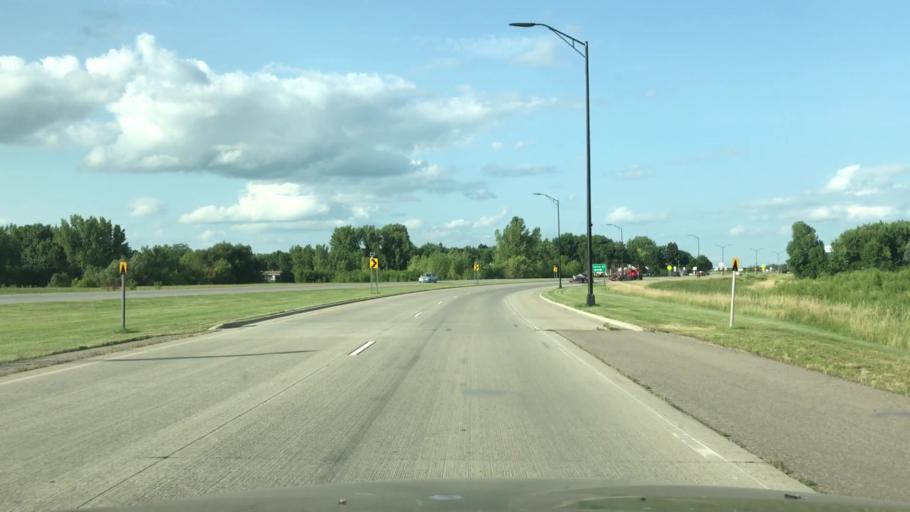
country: US
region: Minnesota
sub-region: Nobles County
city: Worthington
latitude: 43.6156
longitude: -95.5892
